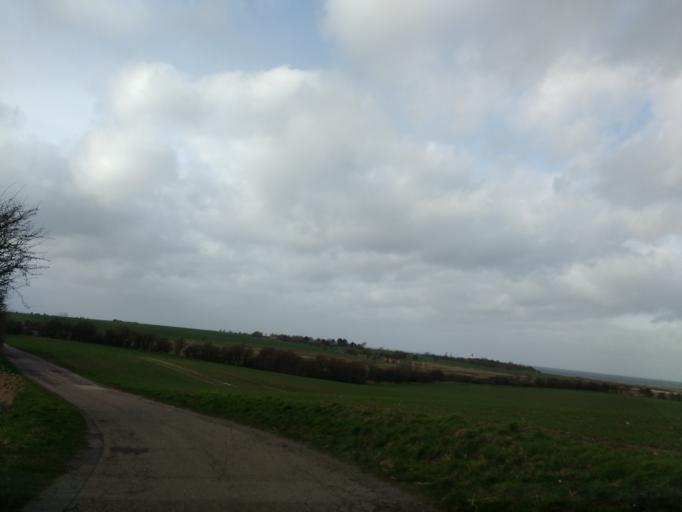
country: DE
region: Schleswig-Holstein
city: Heiligenhafen
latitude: 54.3725
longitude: 10.9462
